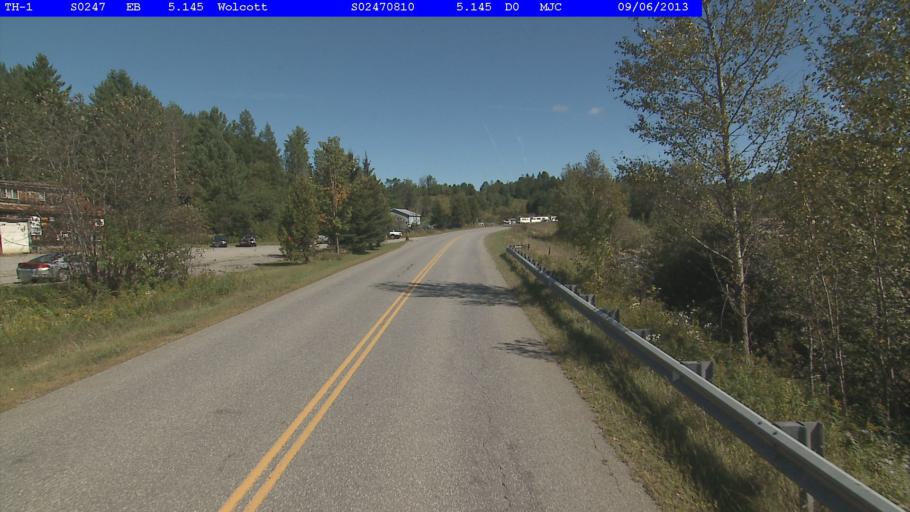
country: US
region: Vermont
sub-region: Caledonia County
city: Hardwick
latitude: 44.6190
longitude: -72.4456
